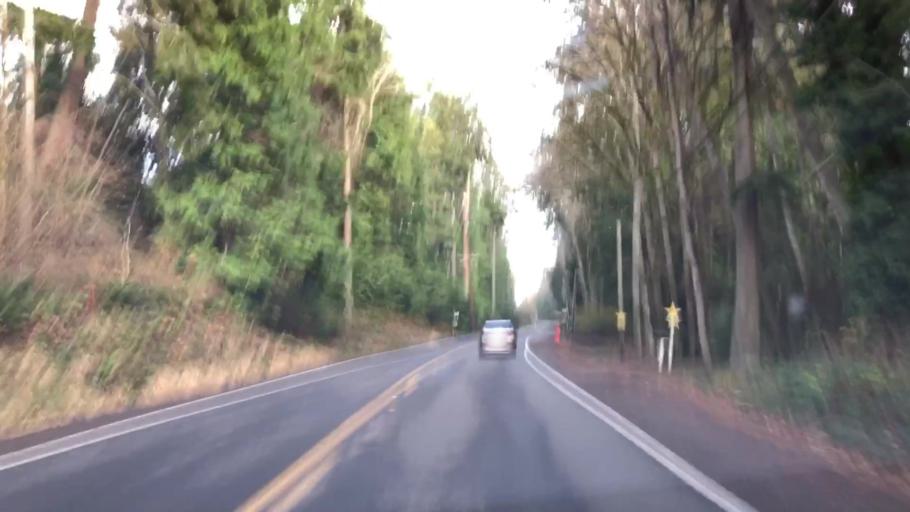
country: US
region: Washington
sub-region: Kitsap County
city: Suquamish
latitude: 47.7522
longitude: -122.5628
